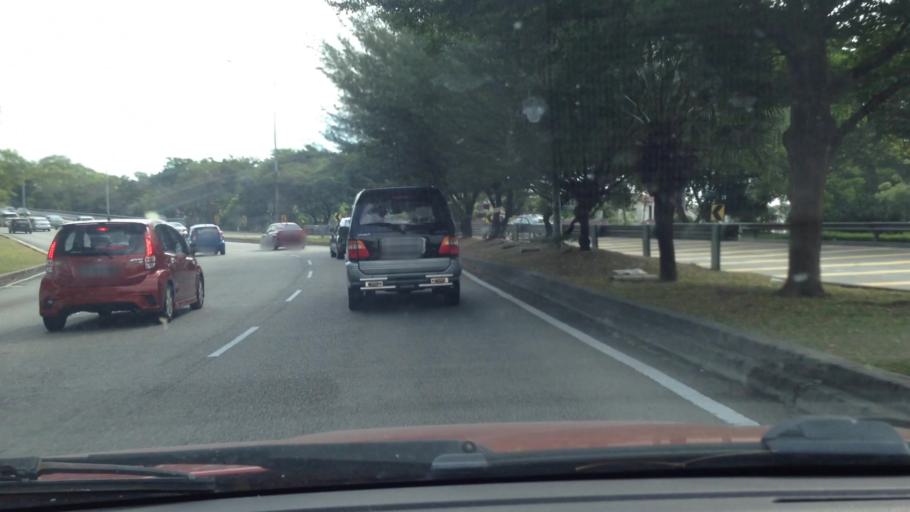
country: MY
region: Selangor
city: Subang Jaya
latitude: 3.0600
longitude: 101.5801
